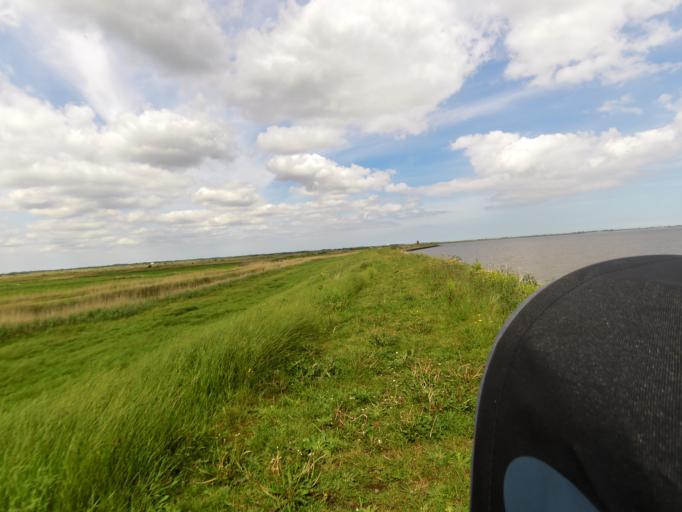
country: GB
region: England
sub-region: Norfolk
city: Great Yarmouth
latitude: 52.5993
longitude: 1.6538
